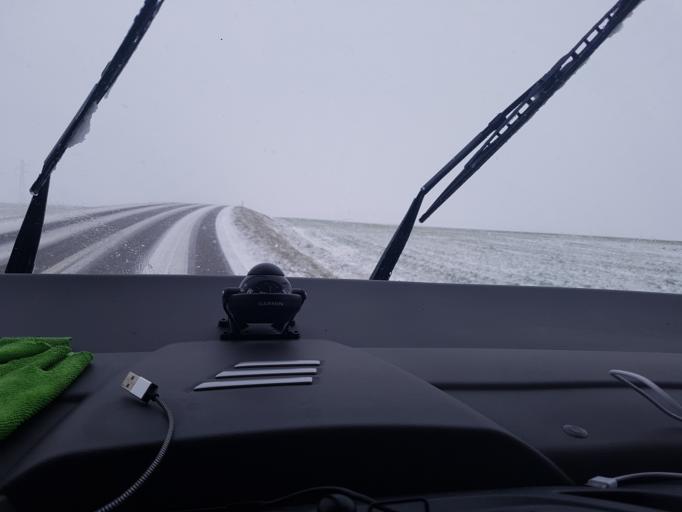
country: FR
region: Lorraine
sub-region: Departement de la Moselle
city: Chateau-Salins
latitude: 48.8382
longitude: 6.4702
